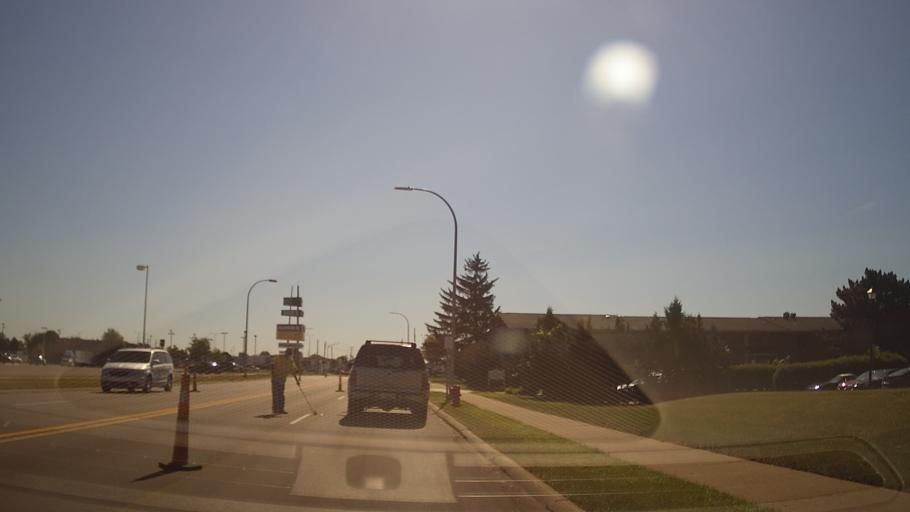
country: US
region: Michigan
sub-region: Macomb County
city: Fraser
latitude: 42.5322
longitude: -82.9171
